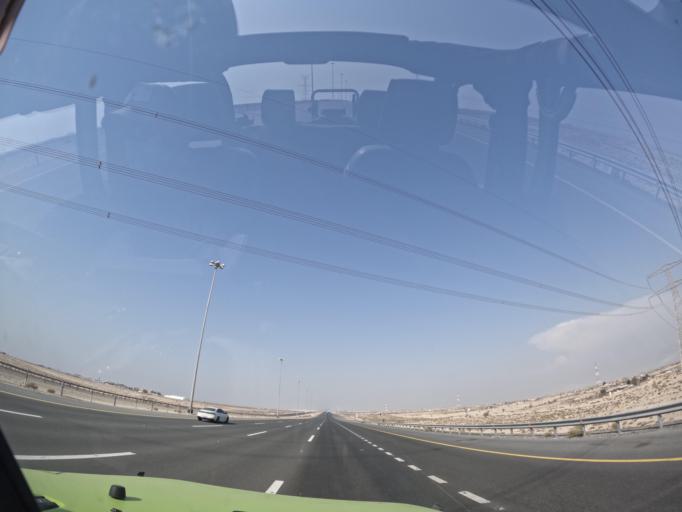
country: AE
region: Abu Dhabi
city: Abu Dhabi
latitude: 24.6512
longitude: 54.7947
